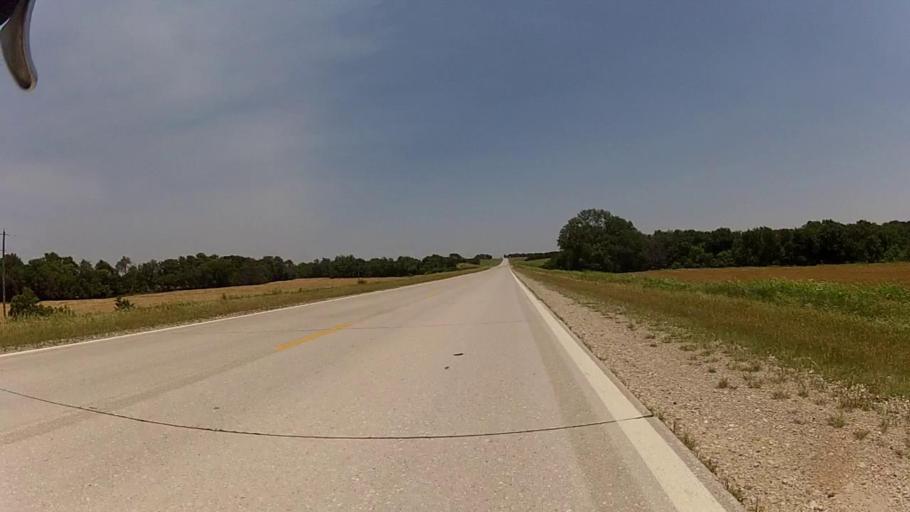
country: US
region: Kansas
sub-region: Sumner County
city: Wellington
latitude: 37.0568
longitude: -97.3709
